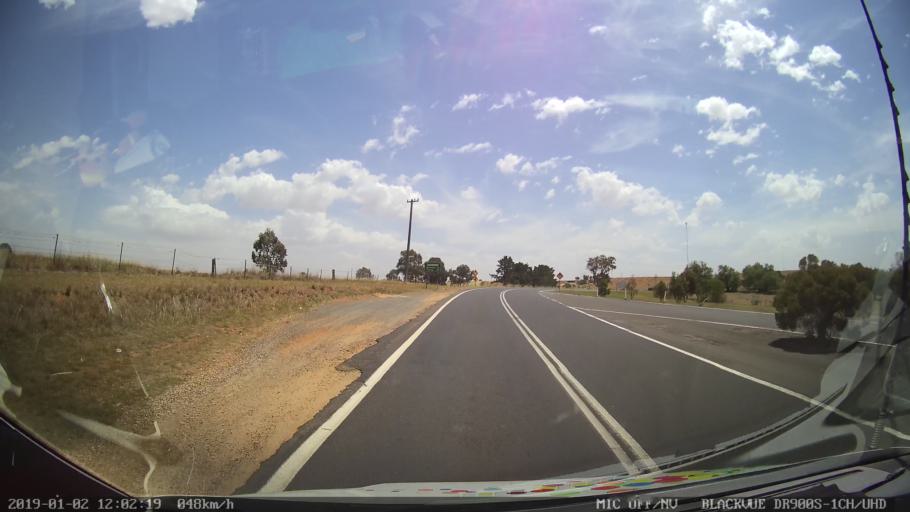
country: AU
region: New South Wales
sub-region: Young
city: Young
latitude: -34.5393
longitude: 148.3243
